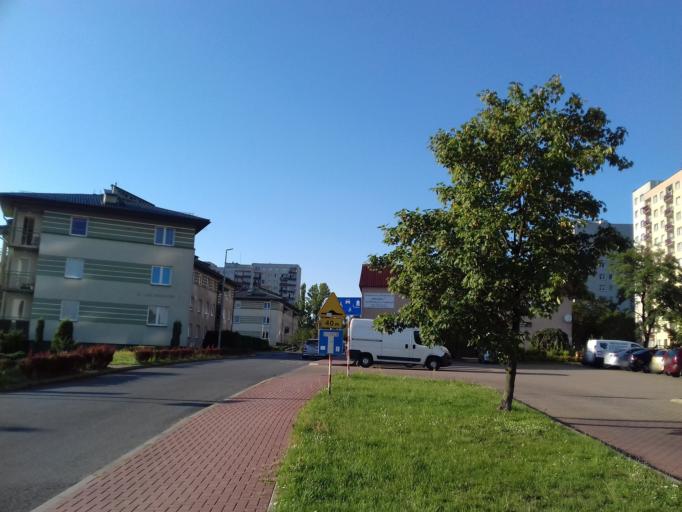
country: PL
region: Silesian Voivodeship
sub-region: Czestochowa
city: Czestochowa
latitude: 50.8411
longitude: 19.1341
